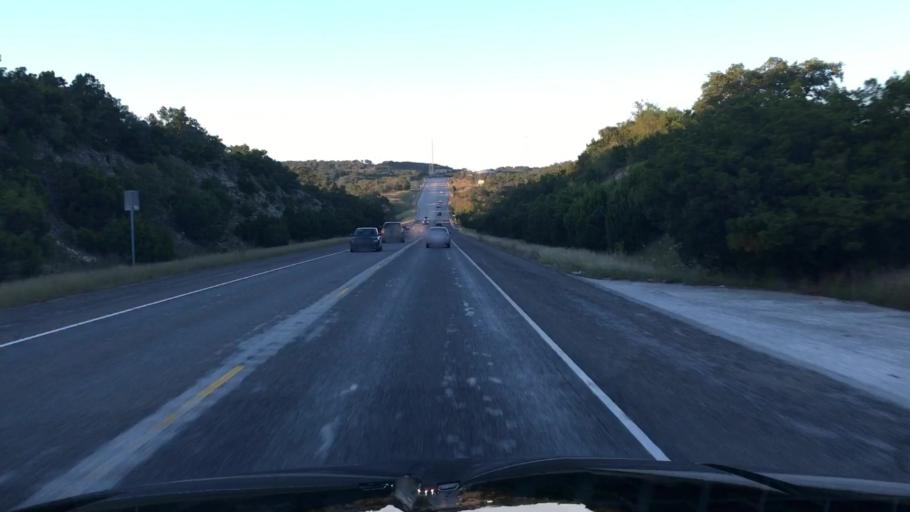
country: US
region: Texas
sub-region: Blanco County
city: Blanco
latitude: 29.9477
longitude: -98.4103
